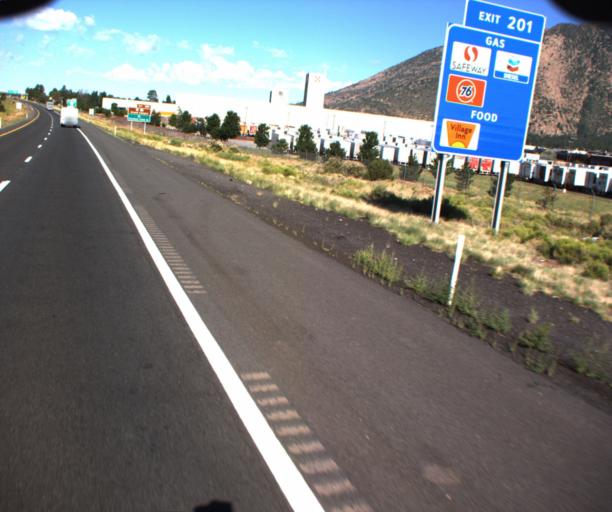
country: US
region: Arizona
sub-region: Coconino County
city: Flagstaff
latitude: 35.2188
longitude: -111.5694
